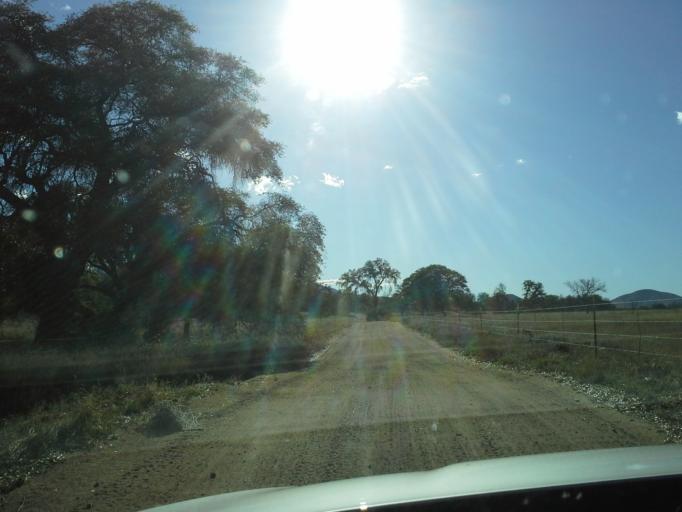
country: US
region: Arizona
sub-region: Pima County
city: Corona de Tucson
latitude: 31.7459
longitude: -110.6983
